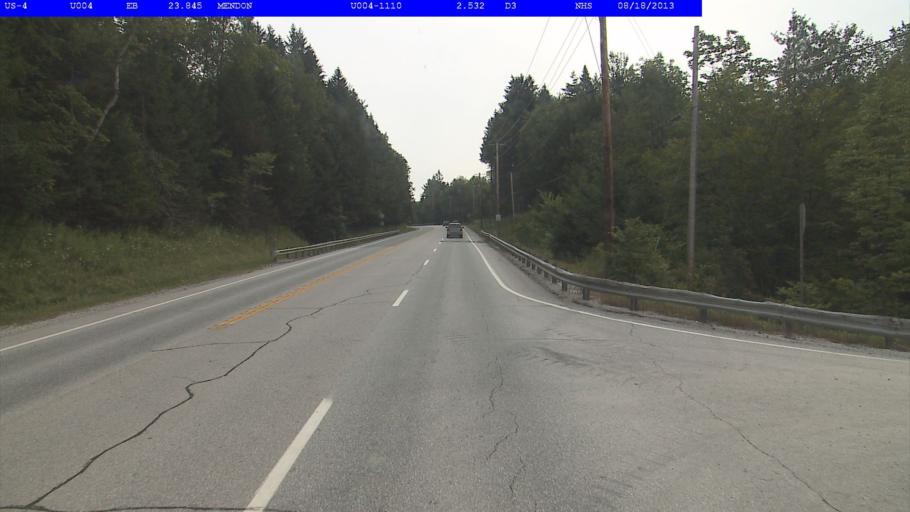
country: US
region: Vermont
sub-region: Rutland County
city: Rutland
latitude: 43.6482
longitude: -72.9035
